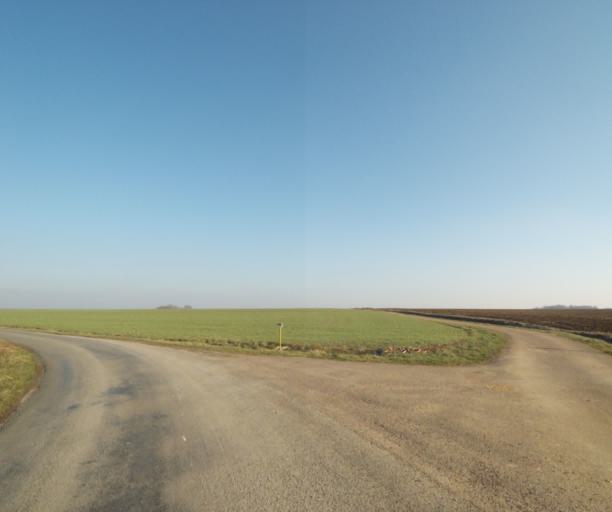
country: FR
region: Champagne-Ardenne
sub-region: Departement de la Haute-Marne
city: Bienville
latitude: 48.5425
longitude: 5.0274
